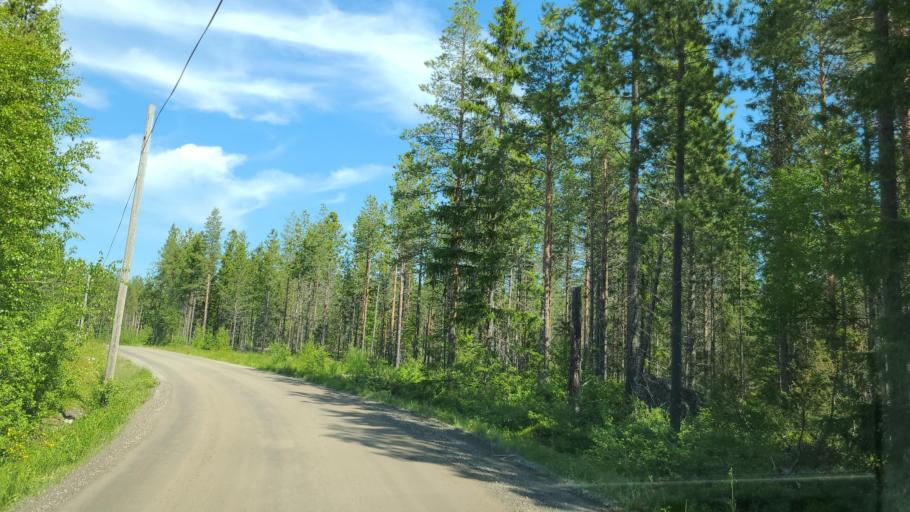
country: SE
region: Vaesterbotten
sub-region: Robertsfors Kommun
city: Robertsfors
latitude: 64.1583
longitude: 20.9418
